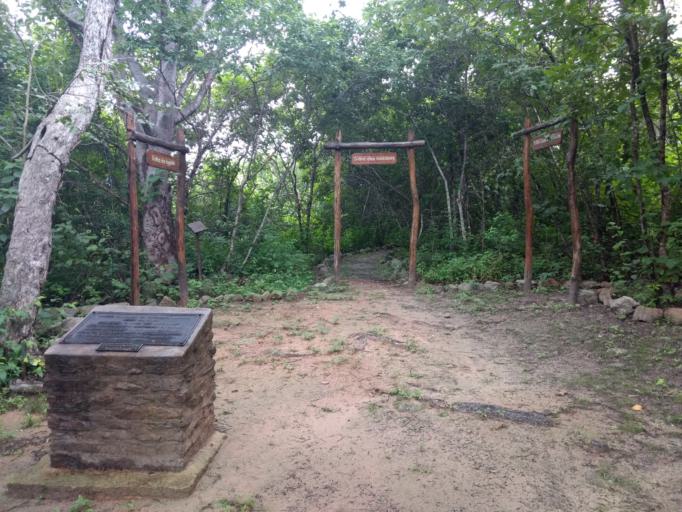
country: BR
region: Ceara
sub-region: Crateus
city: Crateus
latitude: -5.1413
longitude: -40.9160
